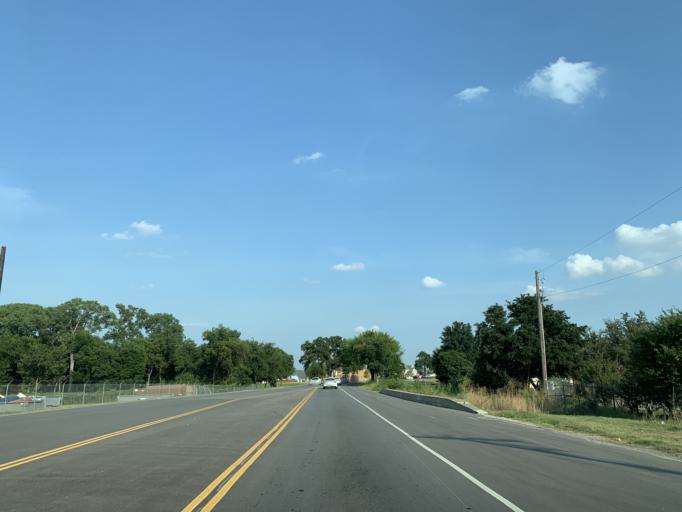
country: US
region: Texas
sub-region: Tarrant County
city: Hurst
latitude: 32.8000
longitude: -97.1801
